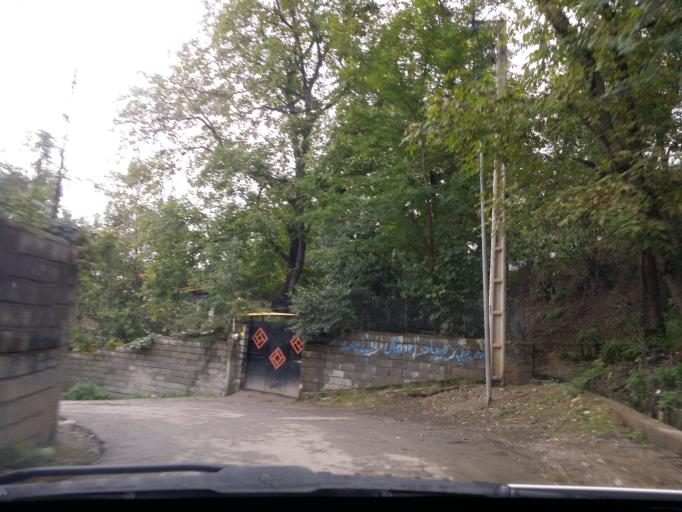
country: IR
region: Mazandaran
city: `Abbasabad
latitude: 36.5040
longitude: 51.1886
